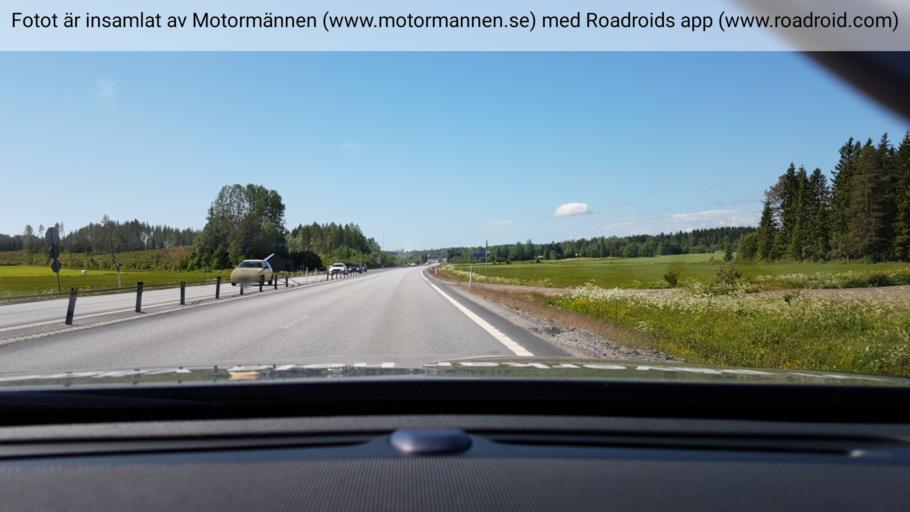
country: SE
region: Vaesterbotten
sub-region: Umea Kommun
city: Roback
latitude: 63.7505
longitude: 20.1489
